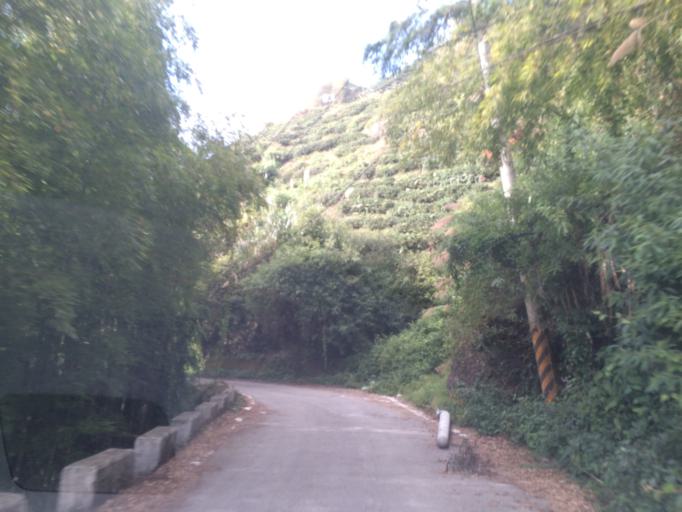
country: TW
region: Taiwan
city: Lugu
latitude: 23.6559
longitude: 120.7770
